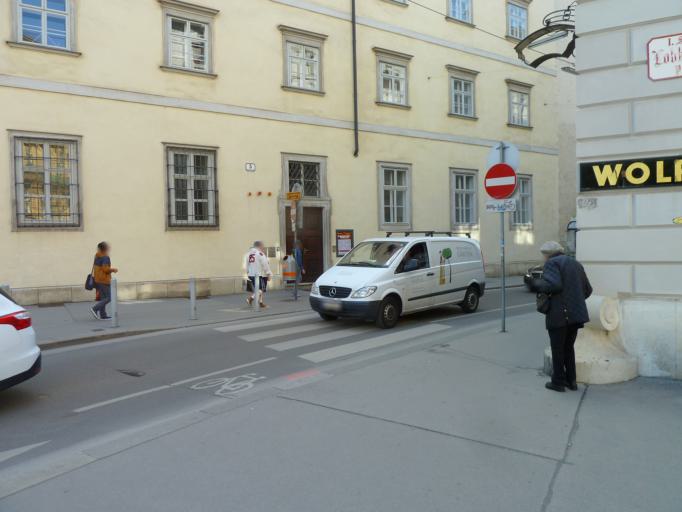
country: AT
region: Vienna
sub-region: Wien Stadt
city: Vienna
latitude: 48.2053
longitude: 16.3683
